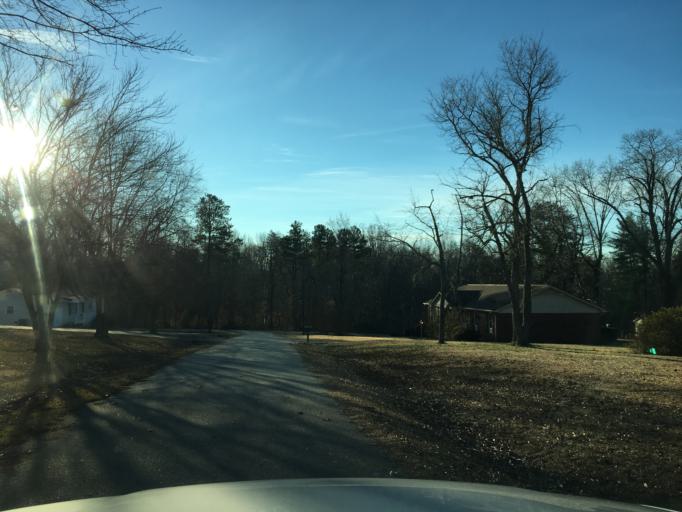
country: US
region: South Carolina
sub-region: Spartanburg County
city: Lyman
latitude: 34.9233
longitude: -82.1244
